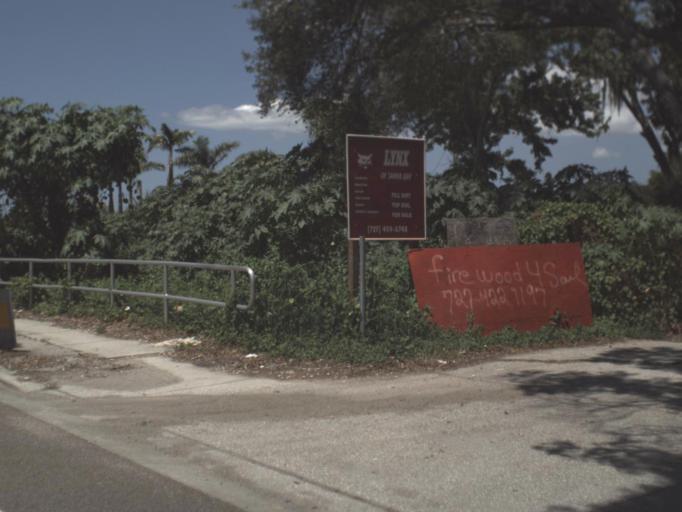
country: US
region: Florida
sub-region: Pinellas County
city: South Highpoint
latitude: 27.8791
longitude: -82.7135
